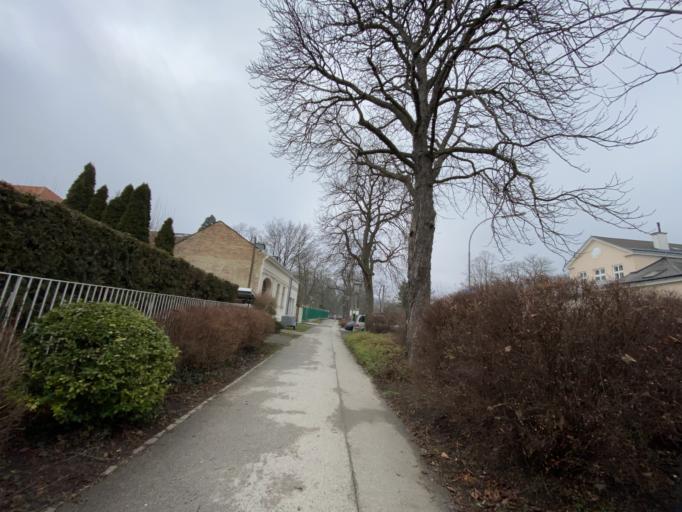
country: AT
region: Lower Austria
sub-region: Politischer Bezirk Baden
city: Baden
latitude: 48.0049
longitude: 16.2178
